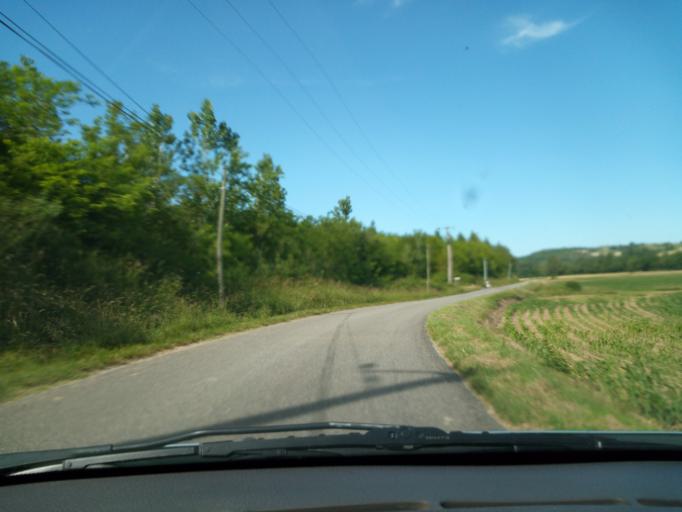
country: FR
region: Midi-Pyrenees
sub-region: Departement du Lot
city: Castelnau-Montratier
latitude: 44.2341
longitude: 1.3312
